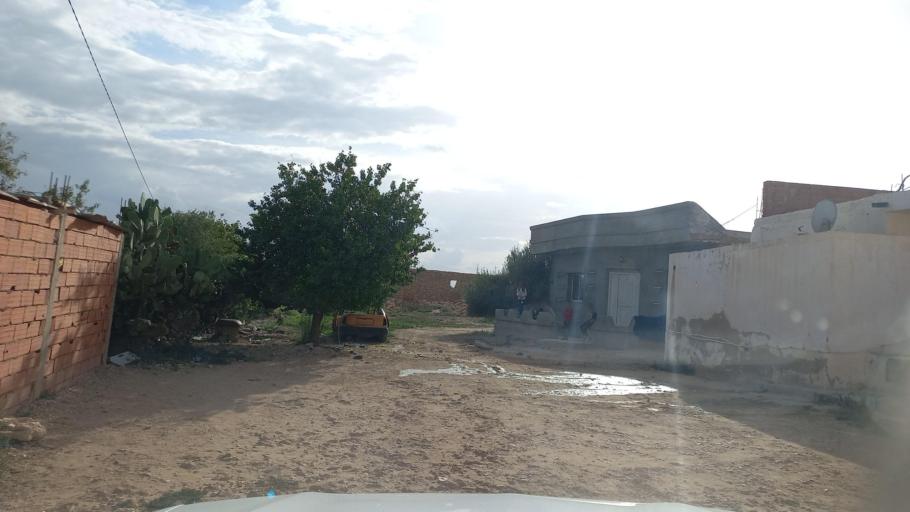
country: TN
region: Al Qasrayn
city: Sbiba
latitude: 35.4451
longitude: 9.0750
